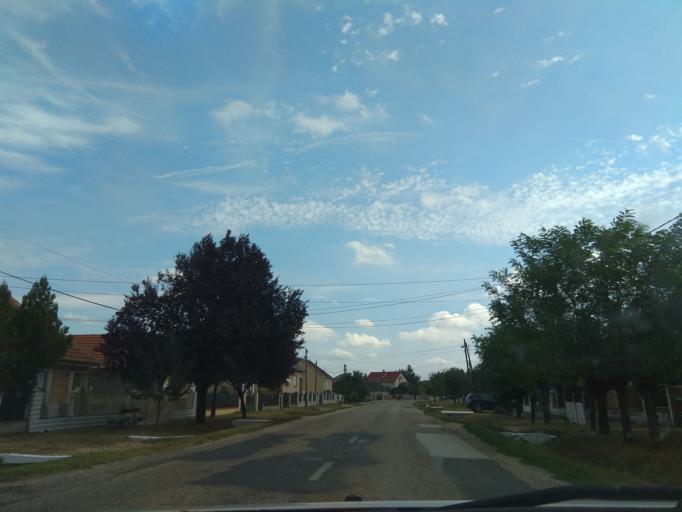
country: HU
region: Borsod-Abauj-Zemplen
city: Sajolad
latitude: 48.0398
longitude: 20.8847
